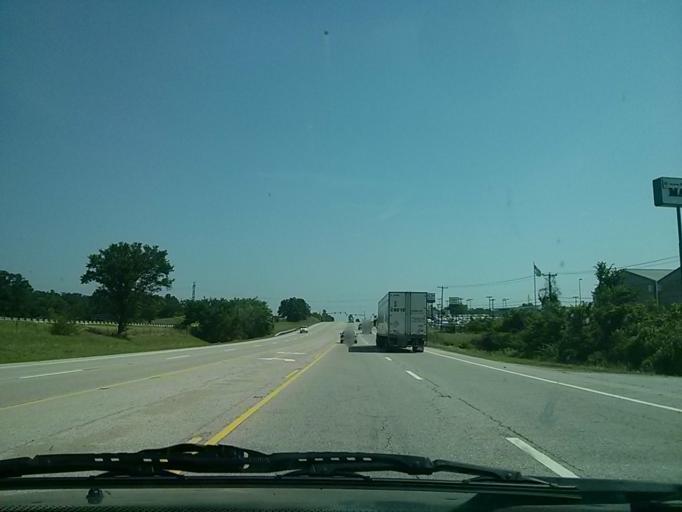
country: US
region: Oklahoma
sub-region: Tulsa County
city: Oakhurst
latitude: 36.0426
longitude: -96.0806
